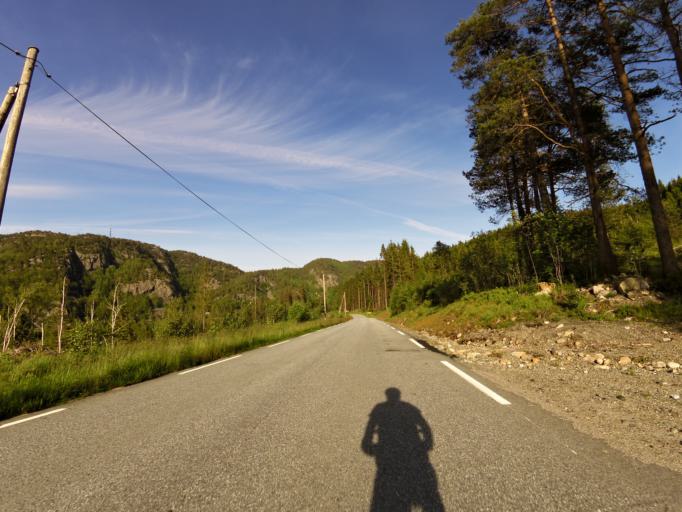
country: NO
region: Vest-Agder
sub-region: Flekkefjord
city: Flekkefjord
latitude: 58.2863
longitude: 6.6041
